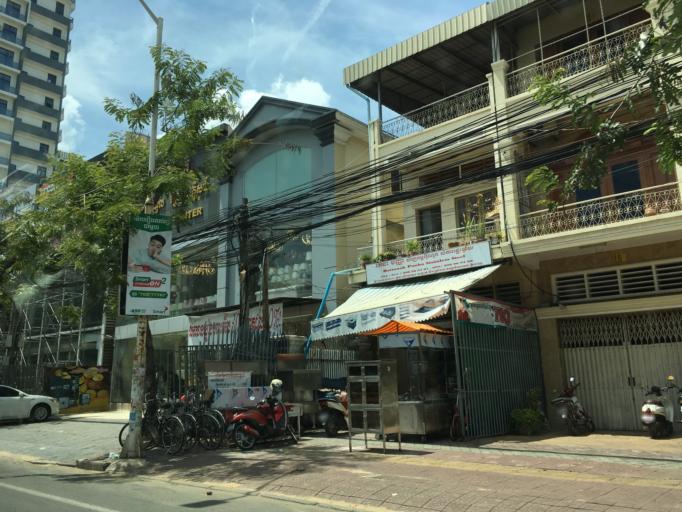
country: KH
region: Phnom Penh
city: Phnom Penh
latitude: 11.5440
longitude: 104.9201
